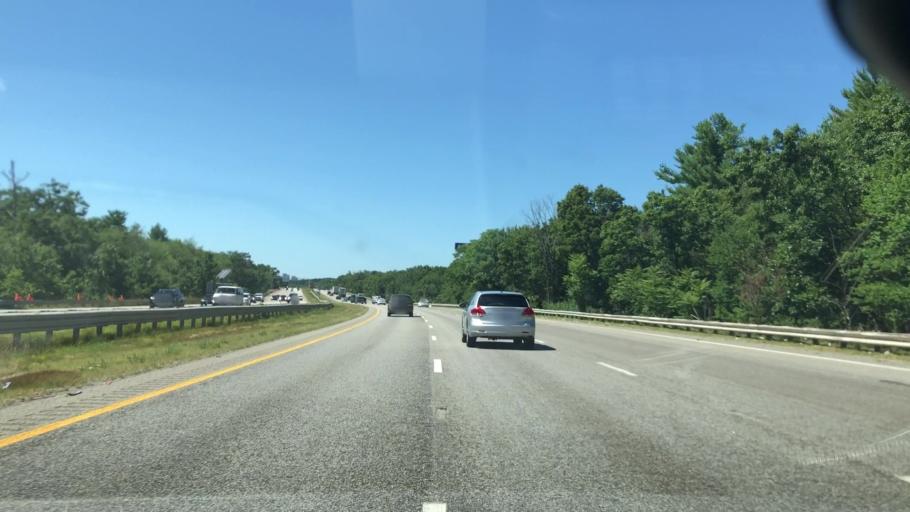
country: US
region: Massachusetts
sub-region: Essex County
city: Methuen
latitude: 42.7385
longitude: -71.2050
